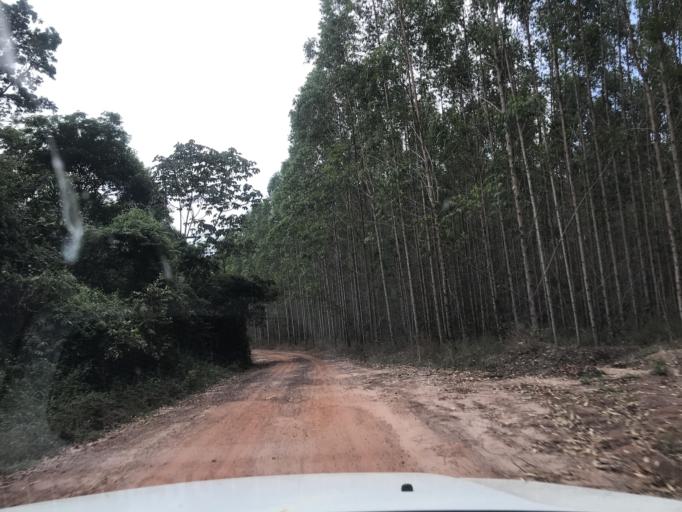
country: BR
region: Bahia
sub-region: Entre Rios
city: Entre Rios
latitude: -12.1009
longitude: -38.1887
